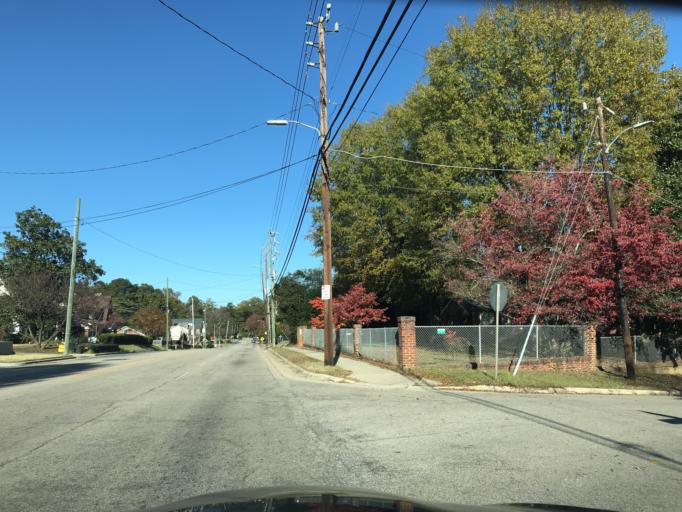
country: US
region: North Carolina
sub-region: Wake County
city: Raleigh
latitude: 35.7943
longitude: -78.6314
